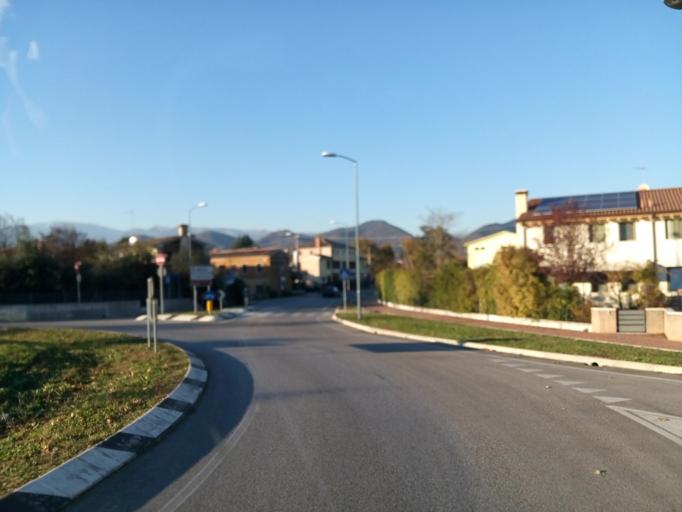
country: IT
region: Veneto
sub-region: Provincia di Treviso
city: Maser
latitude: 45.7912
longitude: 11.9811
